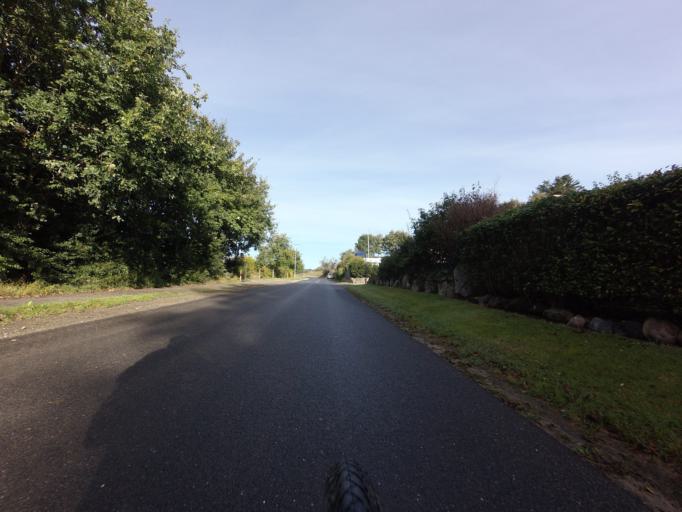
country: DK
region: Central Jutland
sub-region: Viborg Kommune
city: Bjerringbro
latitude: 56.4435
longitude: 9.5570
